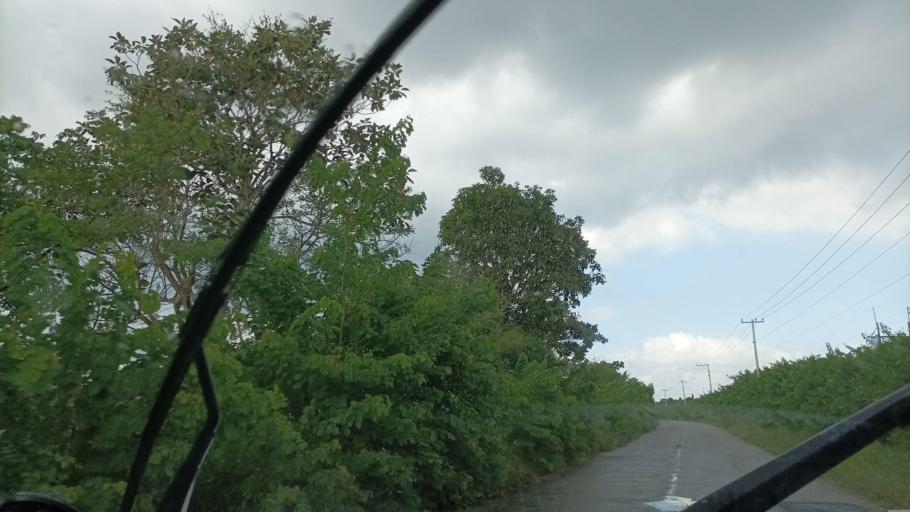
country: MX
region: Veracruz
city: Las Choapas
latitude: 17.8399
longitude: -94.1040
